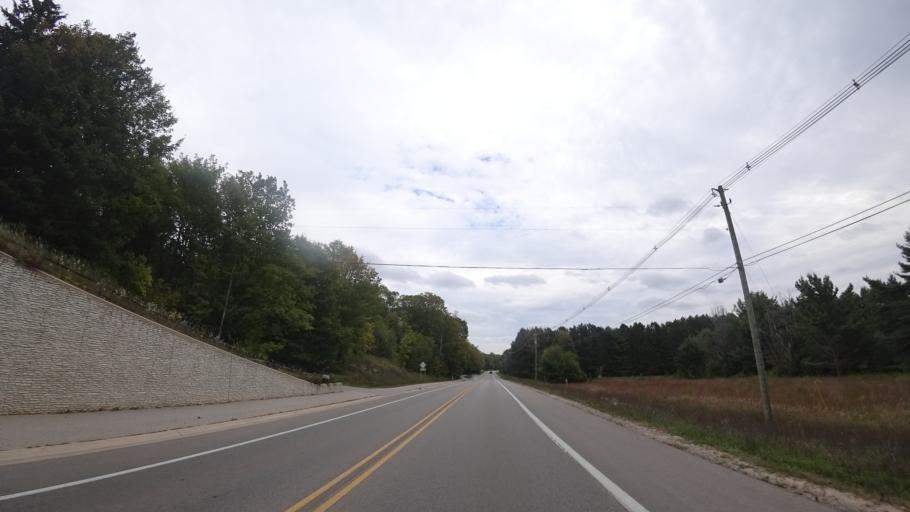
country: US
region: Michigan
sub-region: Emmet County
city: Harbor Springs
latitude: 45.4315
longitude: -84.9424
